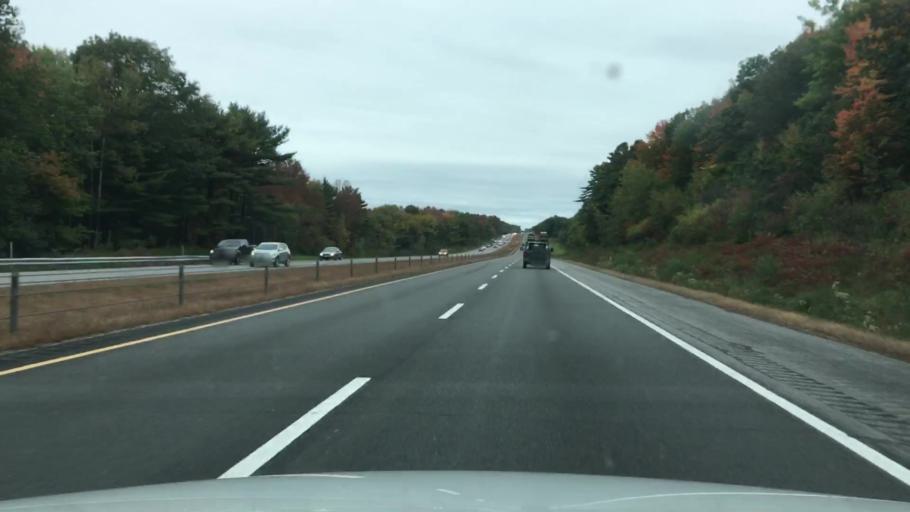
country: US
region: Maine
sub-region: Cumberland County
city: Falmouth Foreside
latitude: 43.7572
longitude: -70.2110
